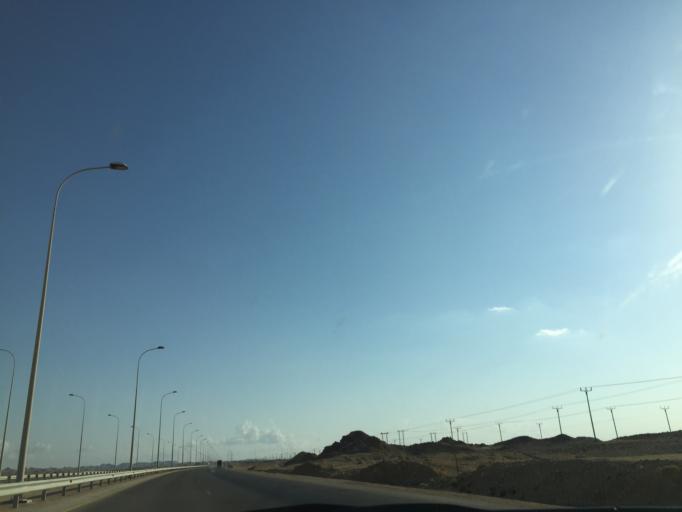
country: OM
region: Zufar
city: Salalah
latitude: 17.5359
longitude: 54.0553
